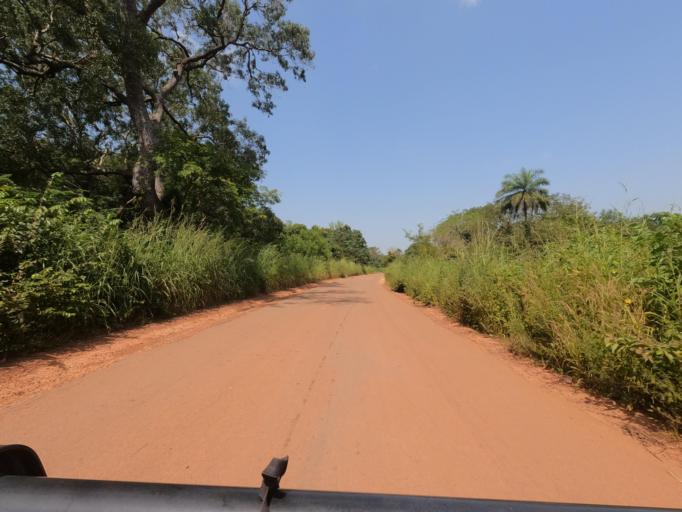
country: GW
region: Oio
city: Bissora
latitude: 12.3599
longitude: -15.7728
